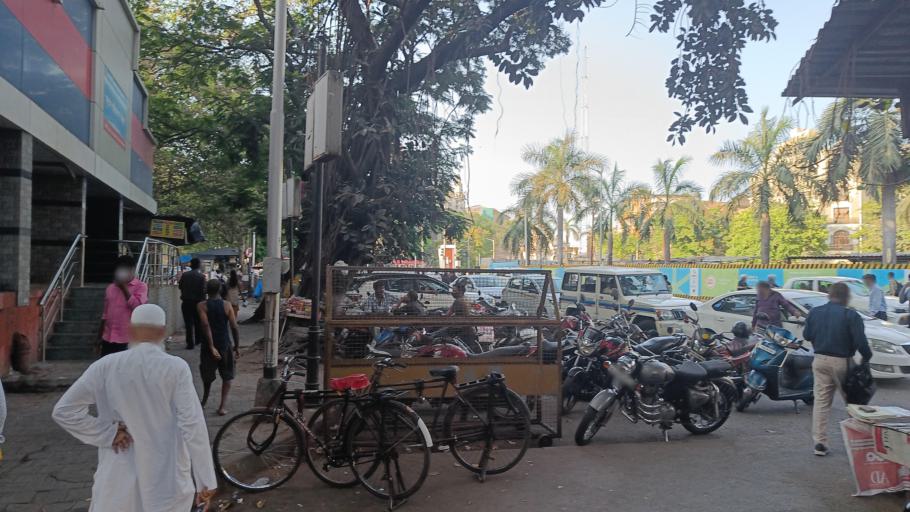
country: IN
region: Maharashtra
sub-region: Raigarh
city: Uran
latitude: 18.9317
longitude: 72.8312
